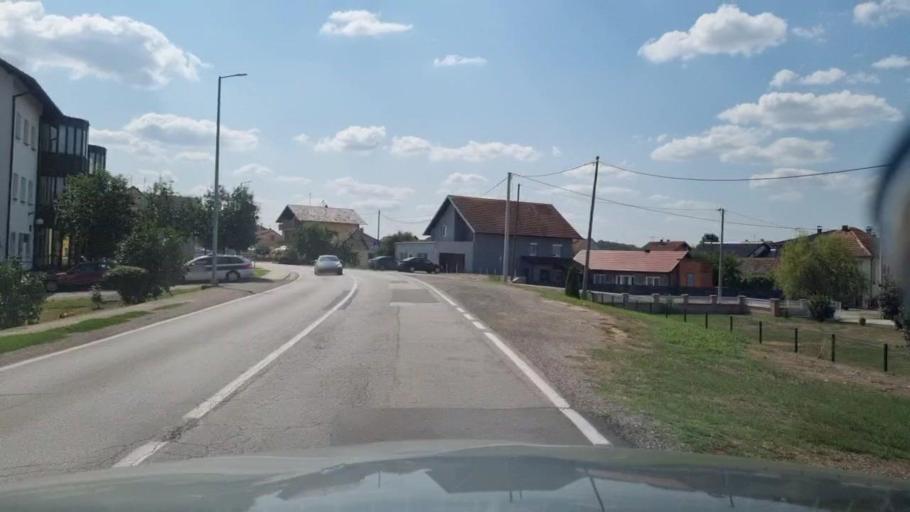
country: HR
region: Vukovarsko-Srijemska
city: Stitar
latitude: 45.0632
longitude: 18.5837
